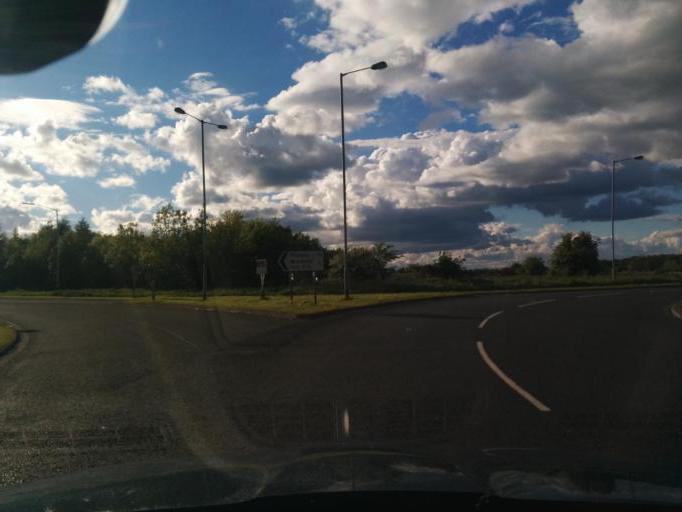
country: GB
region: England
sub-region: Northumberland
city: Bedlington
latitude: 55.1050
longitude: -1.6180
